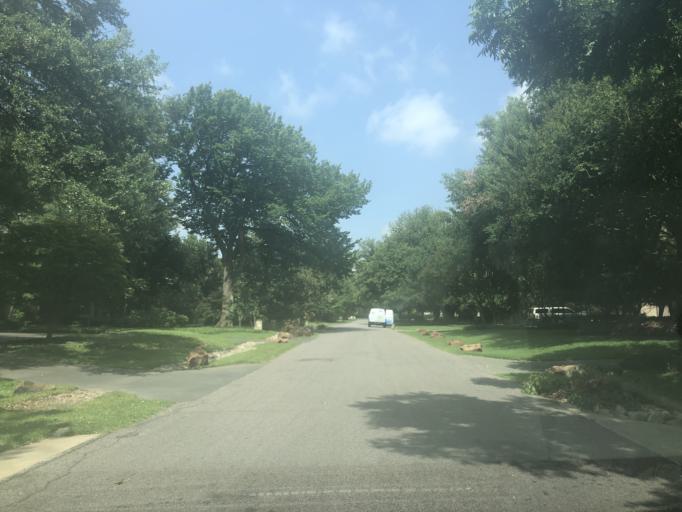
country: US
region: Texas
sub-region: Dallas County
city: University Park
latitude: 32.8676
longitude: -96.8306
